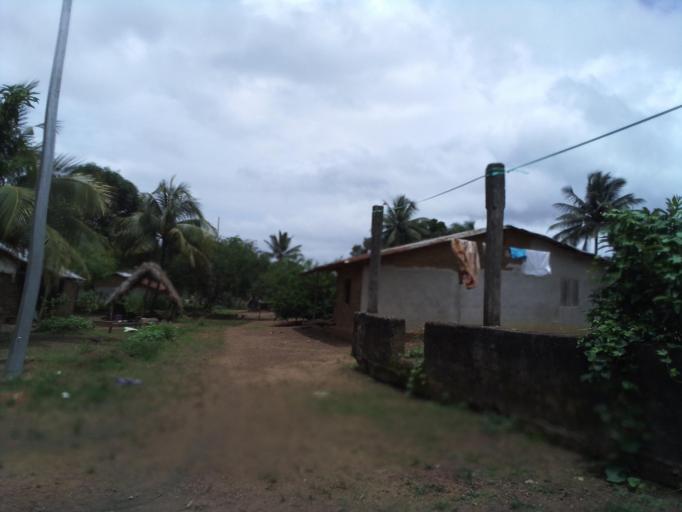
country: SL
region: Eastern Province
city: Kenema
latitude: 7.8137
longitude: -11.1771
